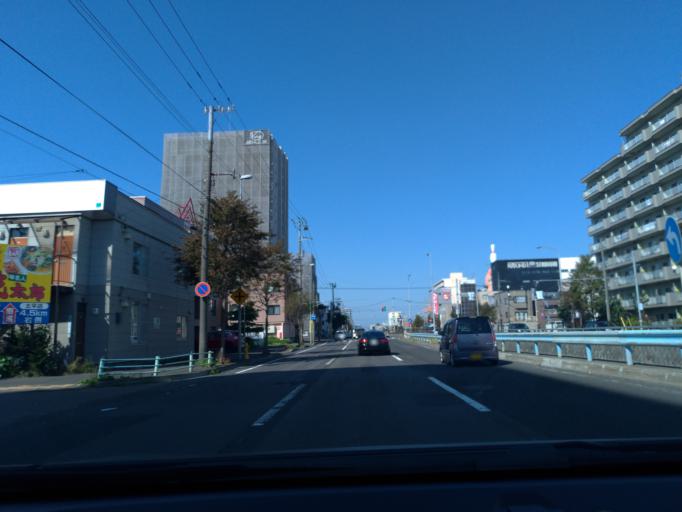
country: JP
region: Hokkaido
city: Sapporo
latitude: 43.0848
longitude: 141.3491
